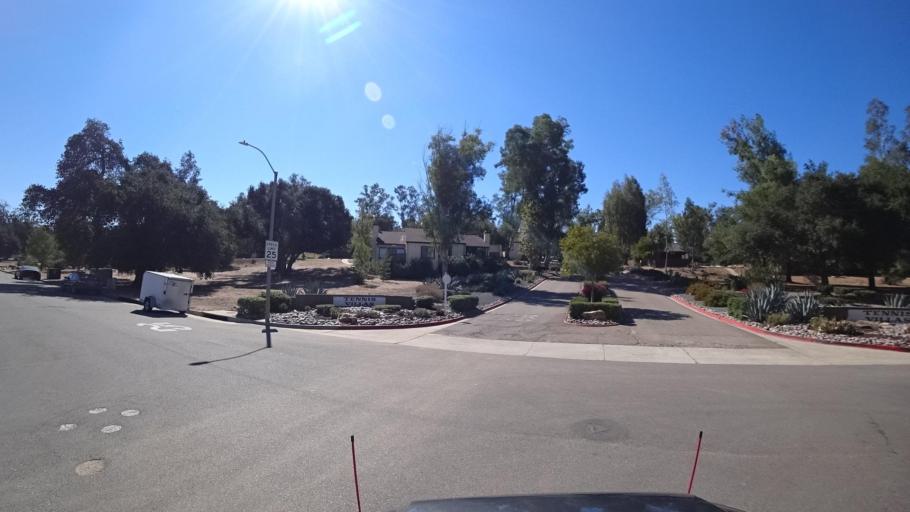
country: US
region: California
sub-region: San Diego County
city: San Diego Country Estates
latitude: 33.0048
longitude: -116.7826
